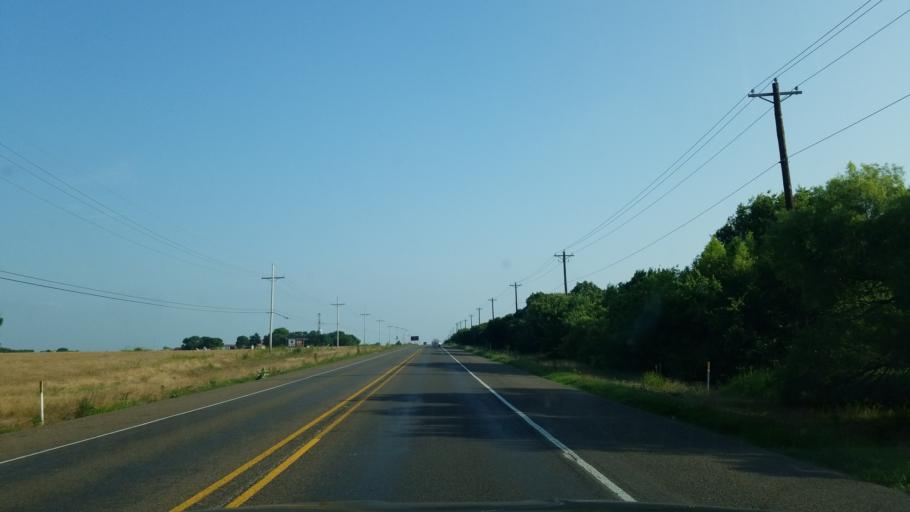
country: US
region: Texas
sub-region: Denton County
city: Pilot Point
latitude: 33.3652
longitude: -96.9648
